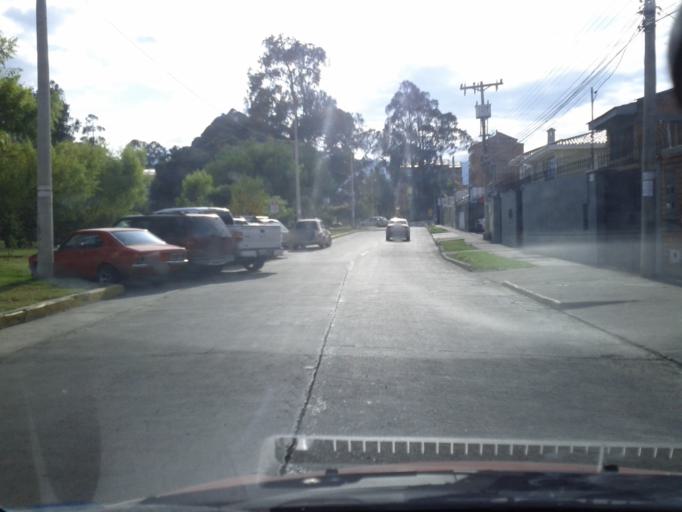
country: EC
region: Azuay
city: Cuenca
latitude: -2.8926
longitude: -79.0192
